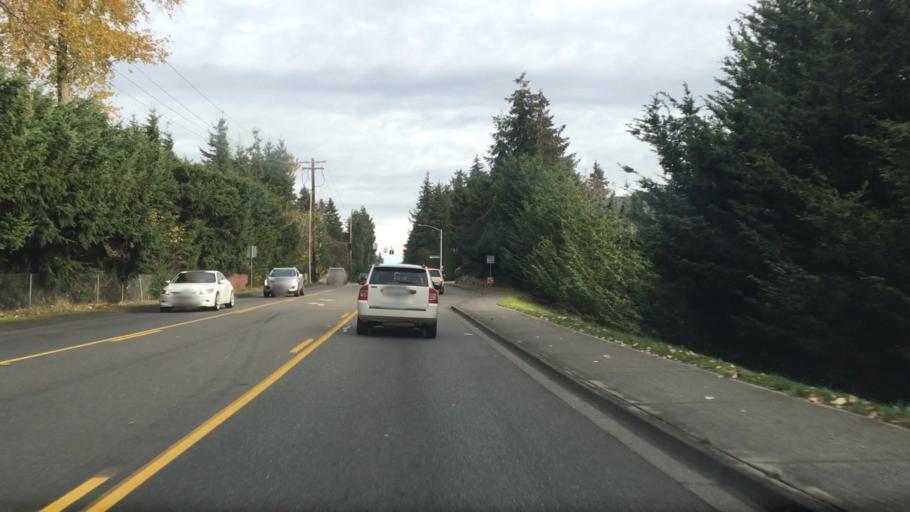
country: US
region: Washington
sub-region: Pierce County
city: South Hill
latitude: 47.1111
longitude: -122.3093
